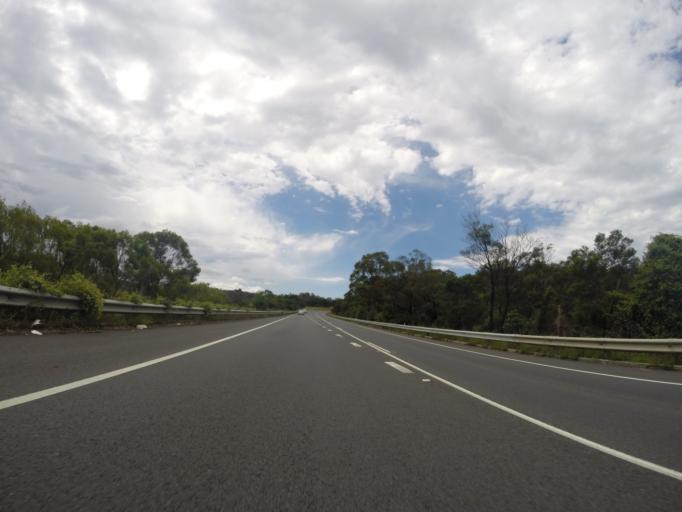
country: AU
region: New South Wales
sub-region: Shoalhaven Shire
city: Milton
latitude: -35.2692
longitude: 150.4244
